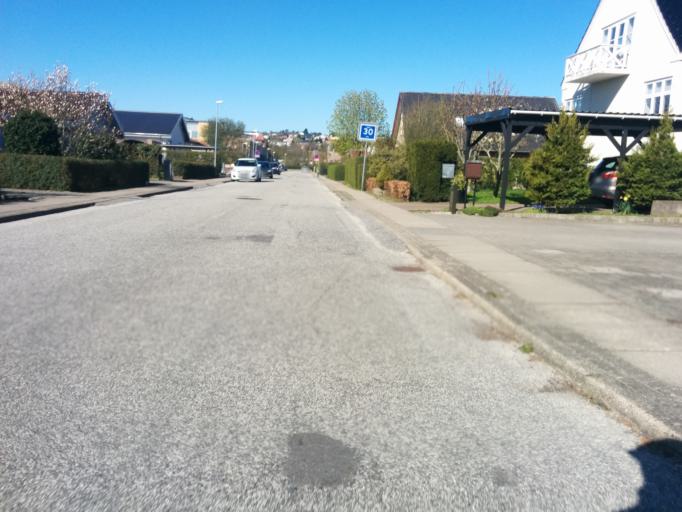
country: DK
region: North Denmark
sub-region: Alborg Kommune
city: Aalborg
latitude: 57.0285
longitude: 9.9193
